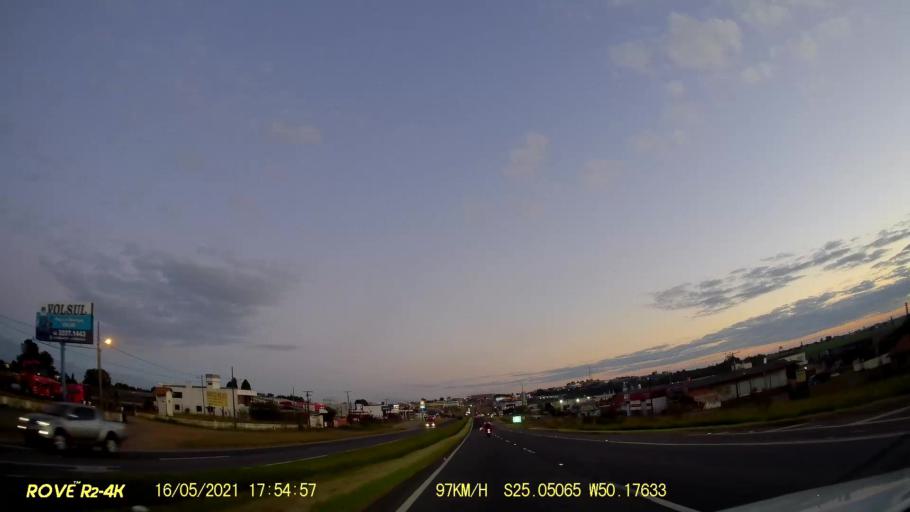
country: BR
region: Parana
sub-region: Ponta Grossa
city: Ponta Grossa
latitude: -25.0508
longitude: -50.1764
